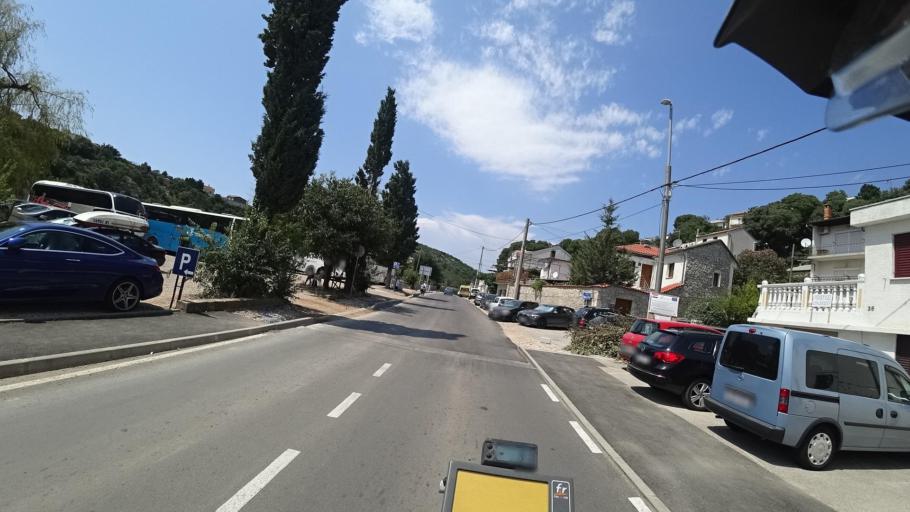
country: HR
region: Primorsko-Goranska
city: Novi Vinodolski
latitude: 45.1301
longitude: 14.7857
